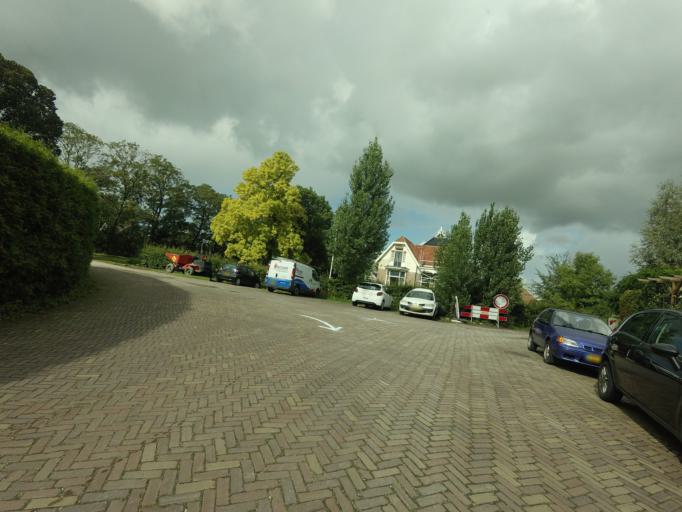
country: NL
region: Friesland
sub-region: Gemeente Boarnsterhim
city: Wergea
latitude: 53.1529
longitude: 5.8421
